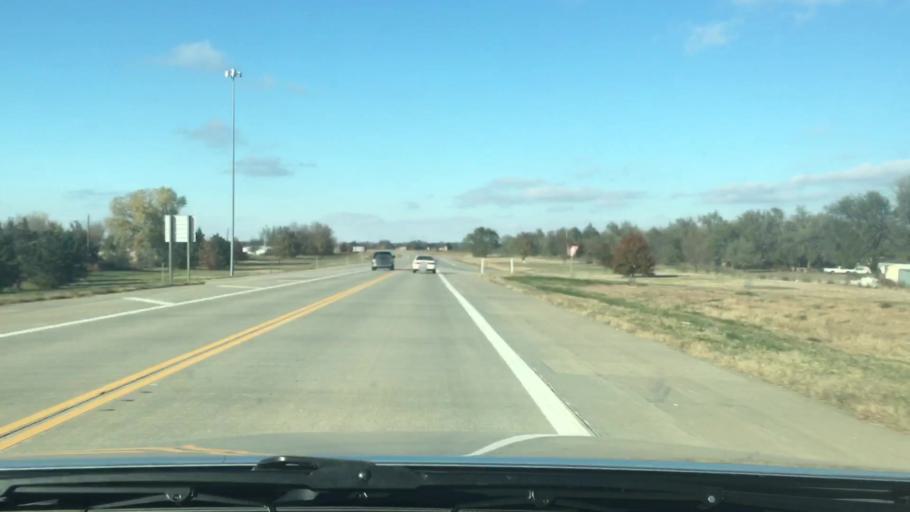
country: US
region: Kansas
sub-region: Reno County
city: South Hutchinson
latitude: 38.0599
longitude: -97.9859
